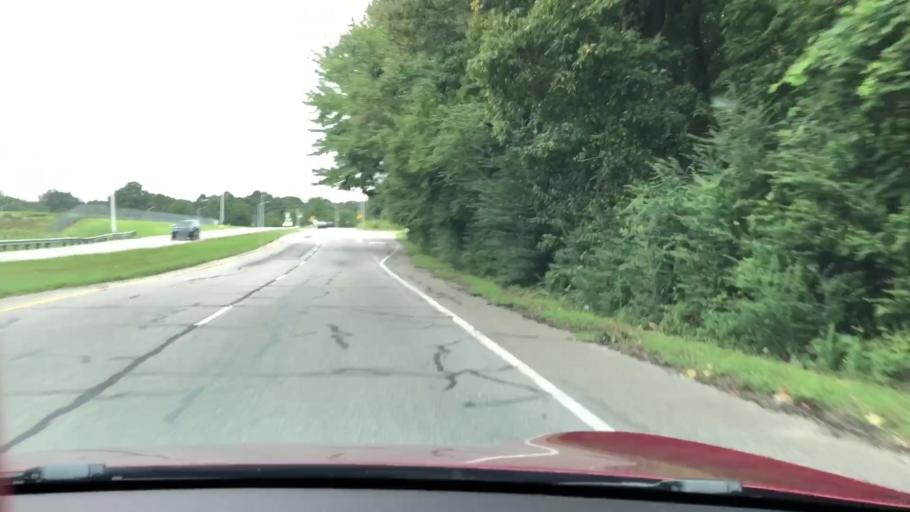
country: US
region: Virginia
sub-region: City of Virginia Beach
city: Virginia Beach
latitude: 36.8346
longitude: -76.0123
